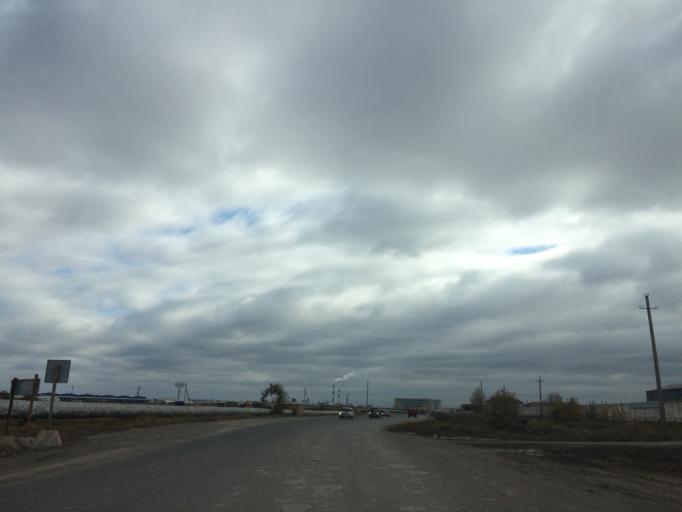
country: KZ
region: Astana Qalasy
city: Astana
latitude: 51.2070
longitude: 71.4522
